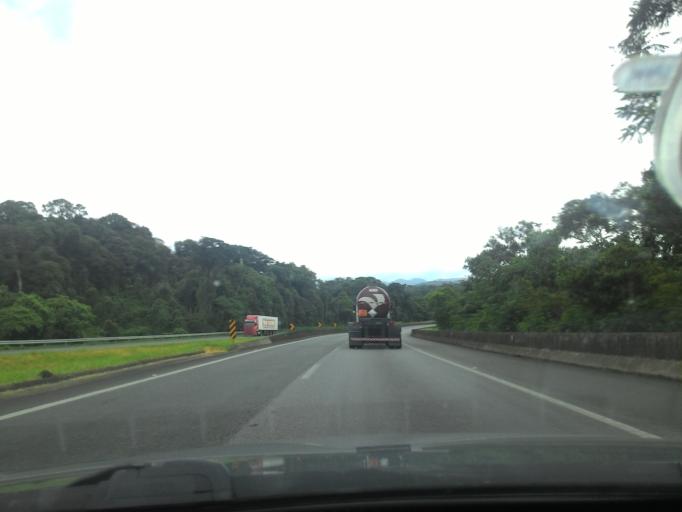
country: BR
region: Sao Paulo
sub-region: Cajati
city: Cajati
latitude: -24.9714
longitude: -48.3987
